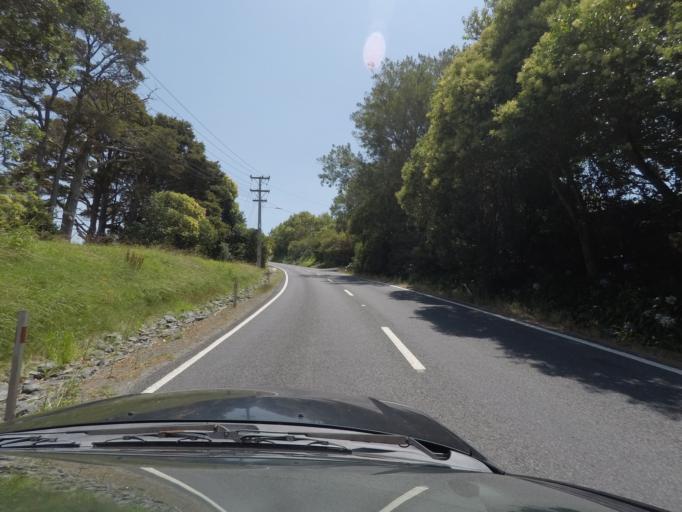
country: NZ
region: Auckland
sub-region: Auckland
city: Warkworth
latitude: -36.3926
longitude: 174.6616
